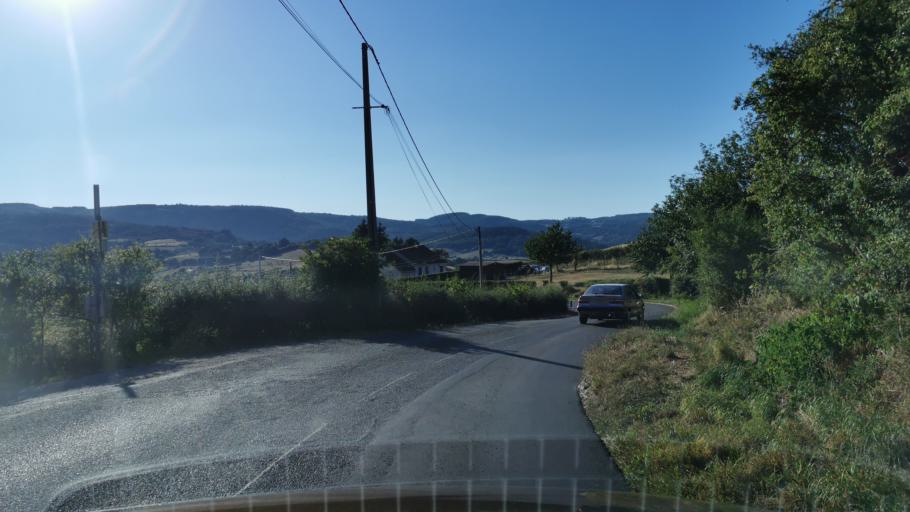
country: FR
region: Bourgogne
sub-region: Departement de Saone-et-Loire
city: Marmagne
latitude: 46.8045
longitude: 4.3388
